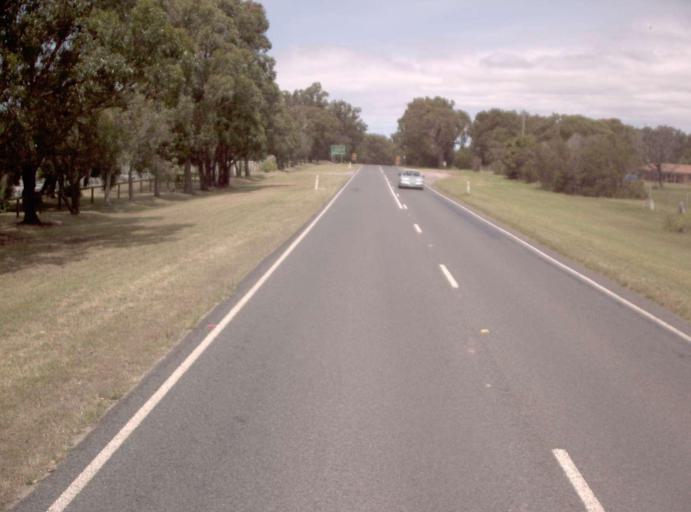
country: AU
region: Victoria
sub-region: Latrobe
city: Traralgon
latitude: -38.5419
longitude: 146.7024
